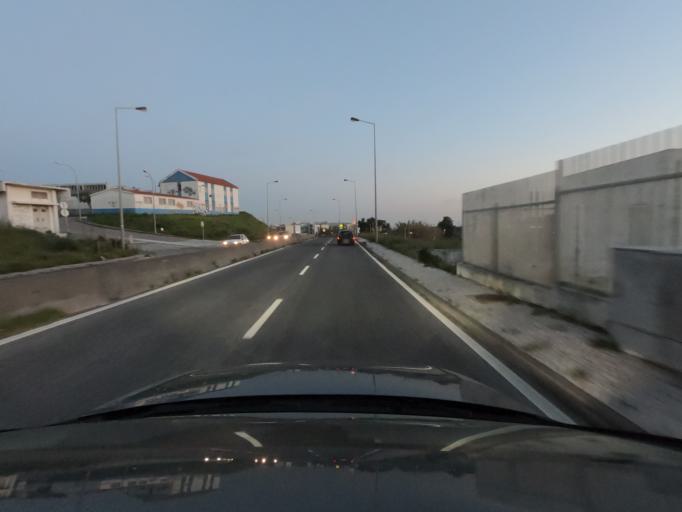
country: PT
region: Lisbon
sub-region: Sintra
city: Cacem
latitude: 38.7534
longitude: -9.3069
